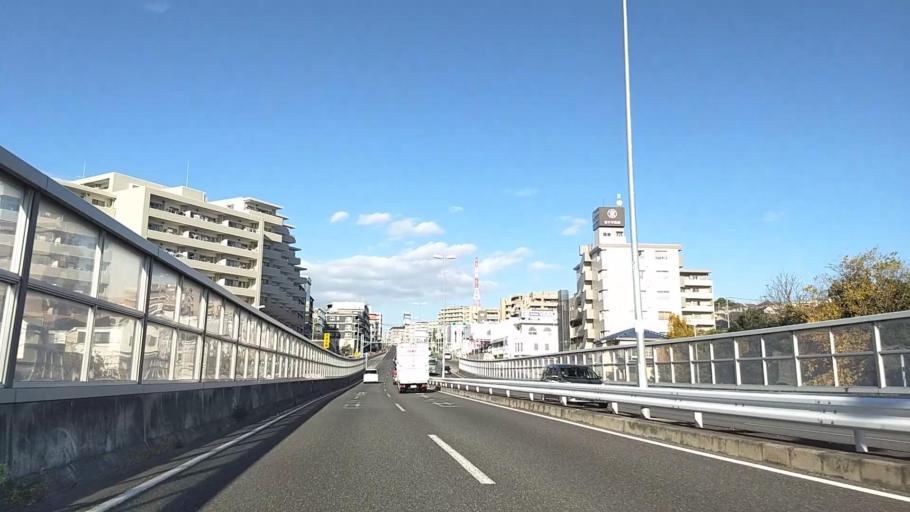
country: JP
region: Tokyo
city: Chofugaoka
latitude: 35.5683
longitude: 139.5648
